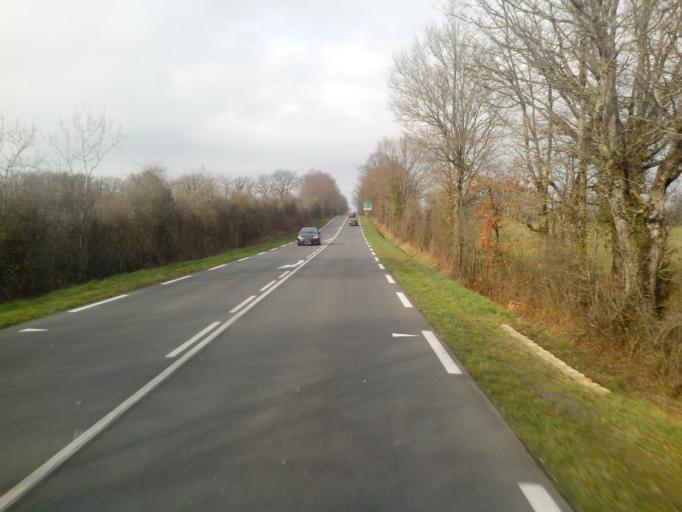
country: FR
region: Limousin
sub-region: Departement de la Haute-Vienne
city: Bussiere-Poitevine
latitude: 46.2754
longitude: 0.8592
